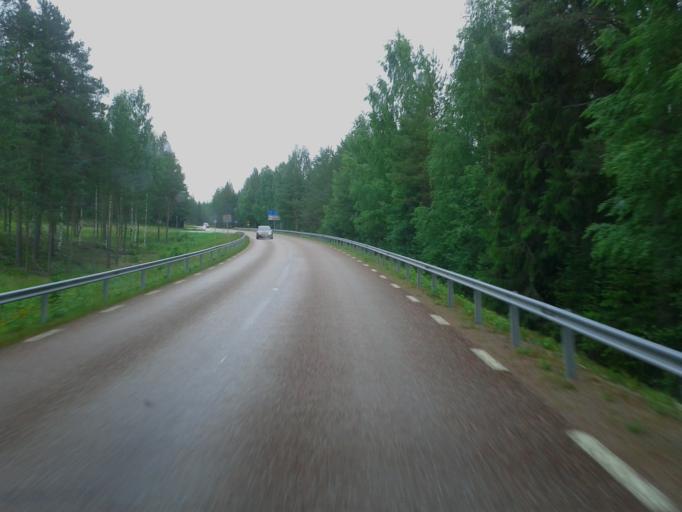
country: NO
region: Hedmark
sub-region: Trysil
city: Innbygda
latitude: 61.7967
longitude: 12.9192
